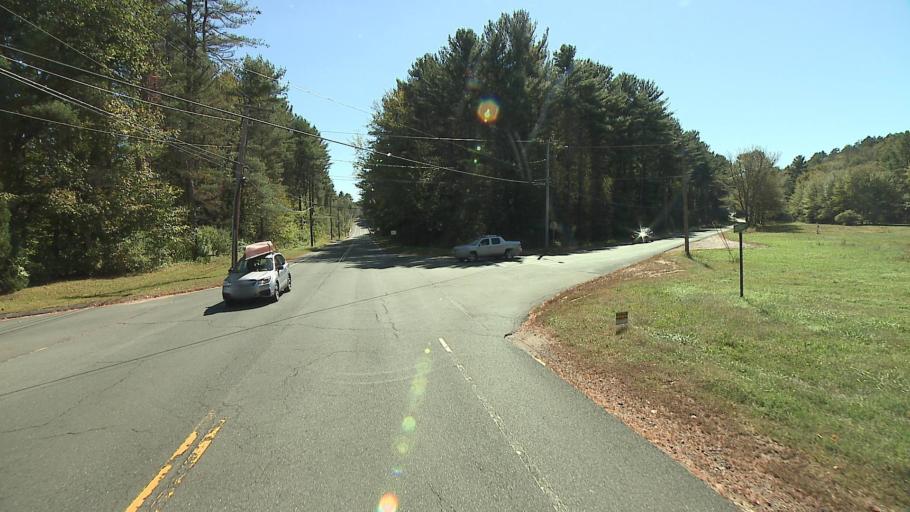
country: US
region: Connecticut
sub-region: Litchfield County
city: New Hartford Center
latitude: 41.8281
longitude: -72.9769
